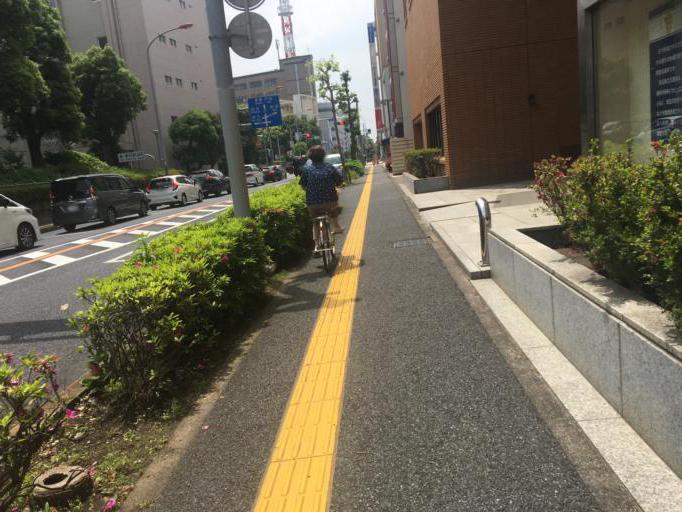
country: JP
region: Saitama
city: Yono
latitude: 35.8574
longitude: 139.6472
